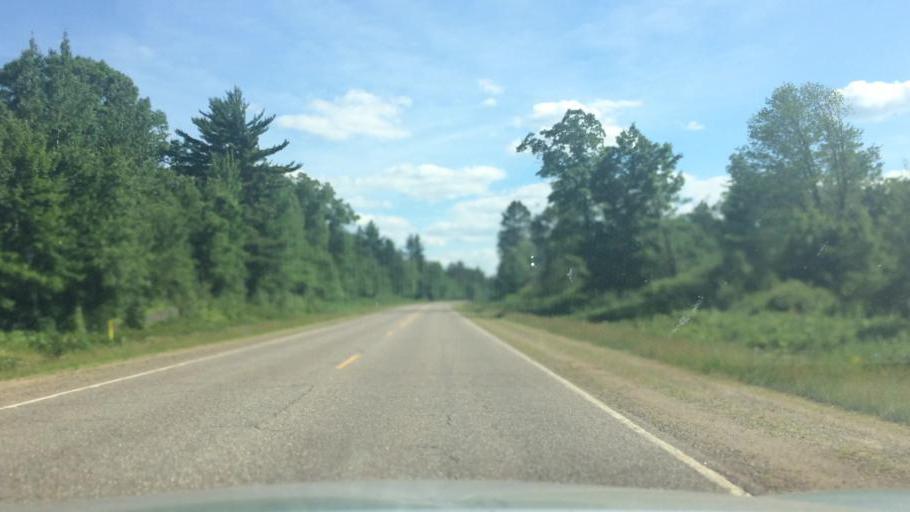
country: US
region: Wisconsin
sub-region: Vilas County
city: Lac du Flambeau
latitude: 46.0782
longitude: -89.6445
